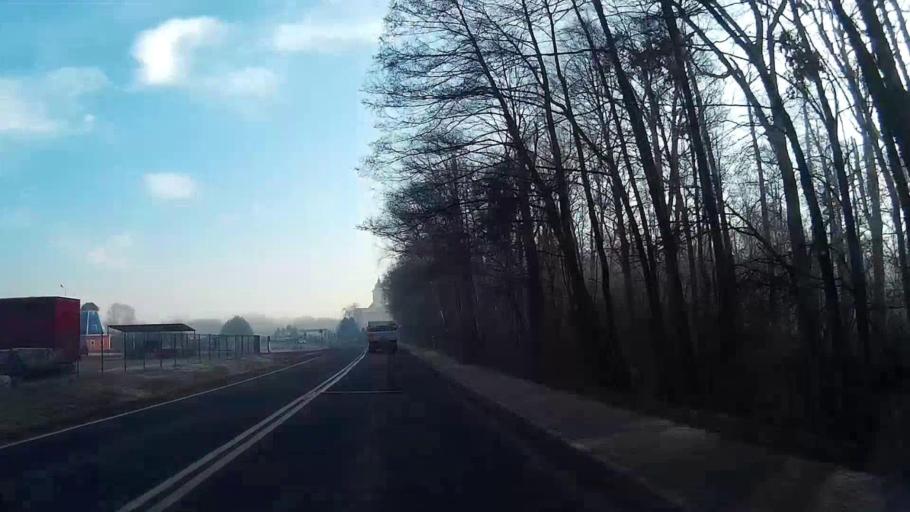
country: PL
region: Lesser Poland Voivodeship
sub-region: Powiat oswiecimski
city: Chelmek
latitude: 50.0714
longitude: 19.2569
